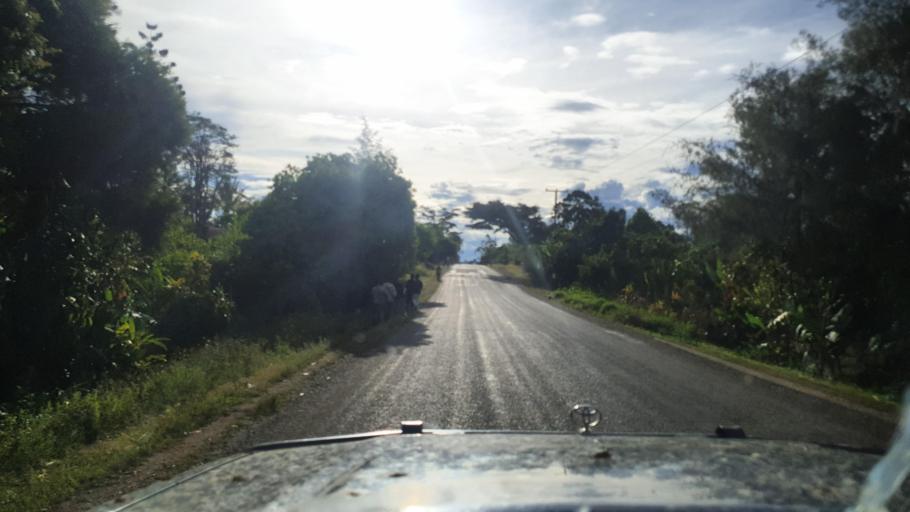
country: PG
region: Jiwaka
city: Minj
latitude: -5.8780
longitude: 144.6729
